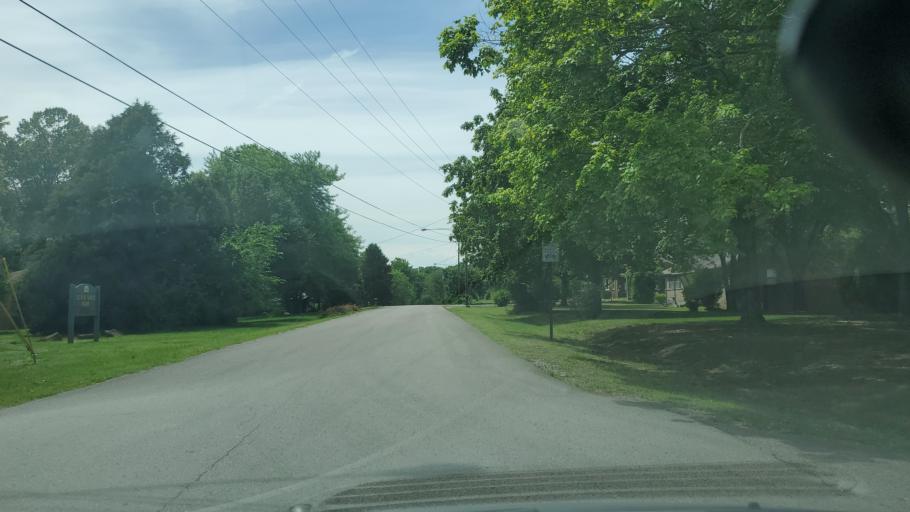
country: US
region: Tennessee
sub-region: Davidson County
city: Oak Hill
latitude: 36.1101
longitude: -86.6957
